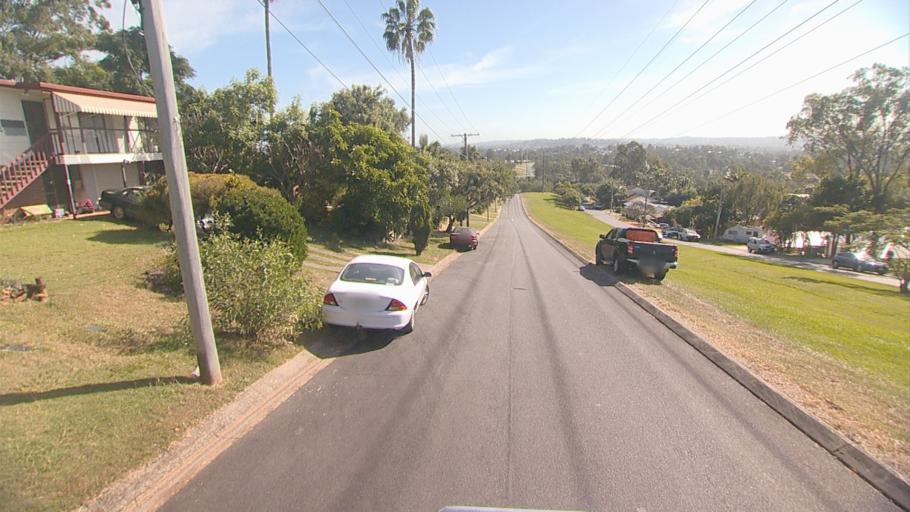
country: AU
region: Queensland
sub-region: Logan
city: Beenleigh
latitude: -27.7081
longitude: 153.1793
